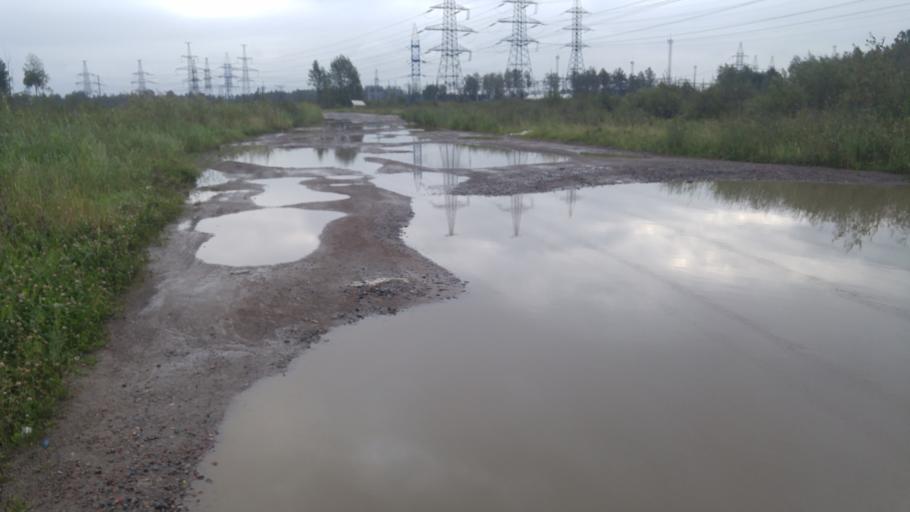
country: RU
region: St.-Petersburg
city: Metallostroy
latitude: 59.7776
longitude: 30.5577
